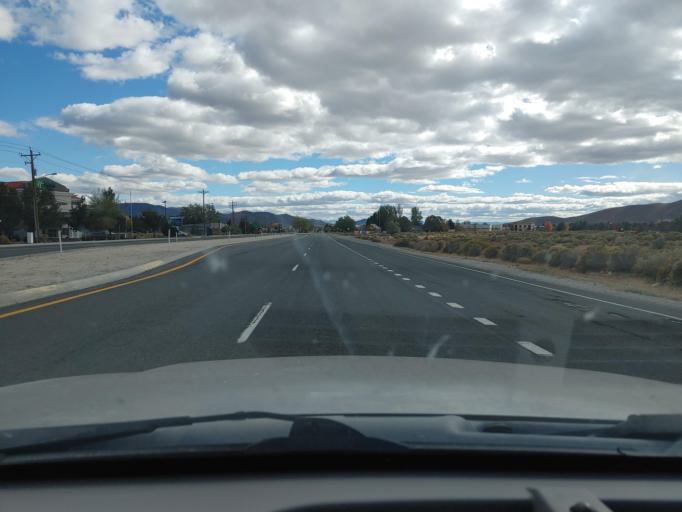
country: US
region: Nevada
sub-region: Carson City
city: Carson City
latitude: 39.1960
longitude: -119.7765
